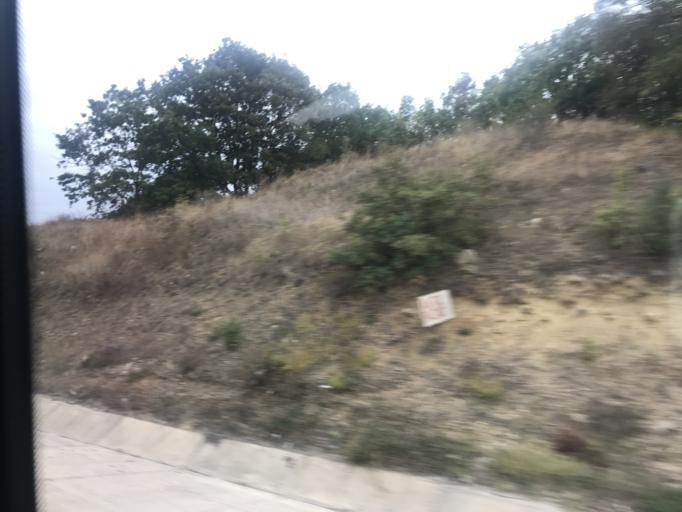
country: TR
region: Balikesir
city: Ergama
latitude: 39.6218
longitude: 27.5851
